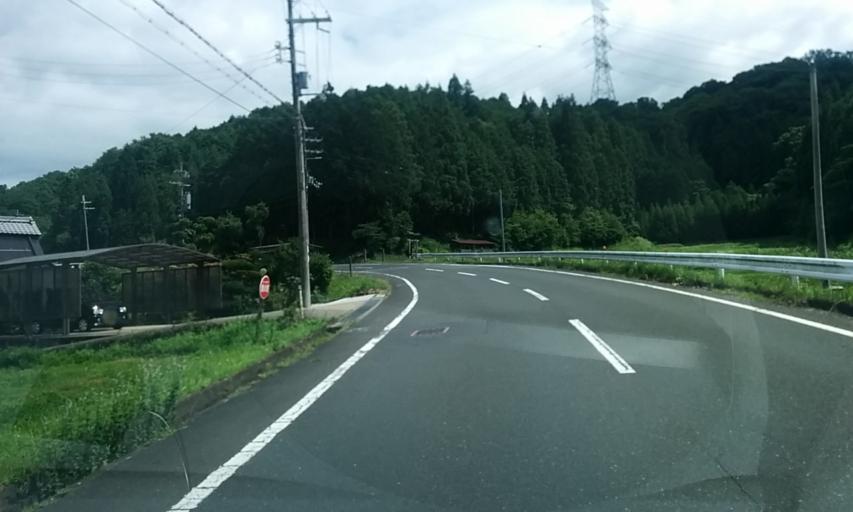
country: JP
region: Kyoto
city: Ayabe
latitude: 35.3531
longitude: 135.2711
